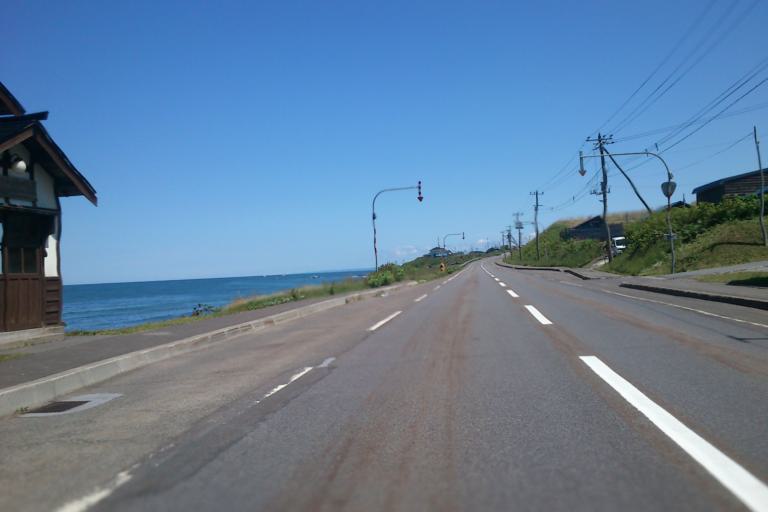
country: JP
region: Hokkaido
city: Rumoi
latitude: 43.8427
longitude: 141.5000
